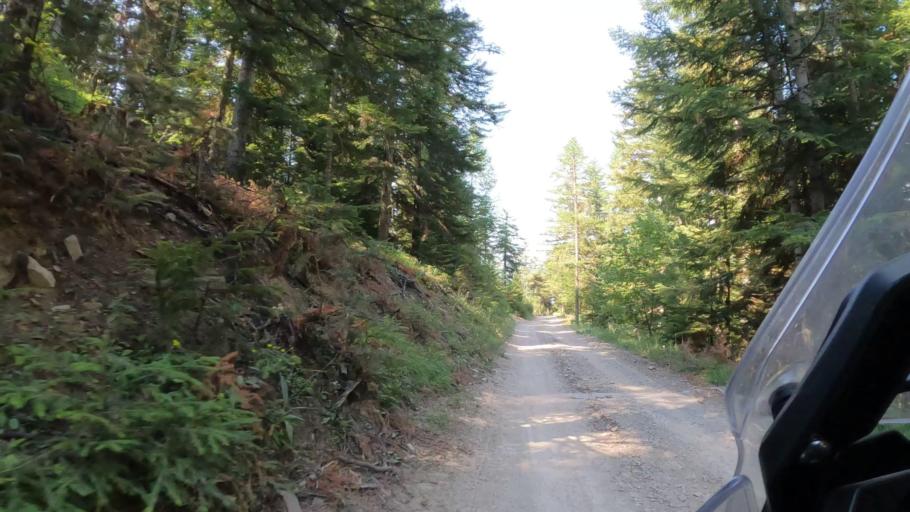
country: FR
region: Provence-Alpes-Cote d'Azur
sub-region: Departement des Hautes-Alpes
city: Embrun
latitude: 44.5953
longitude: 6.5627
